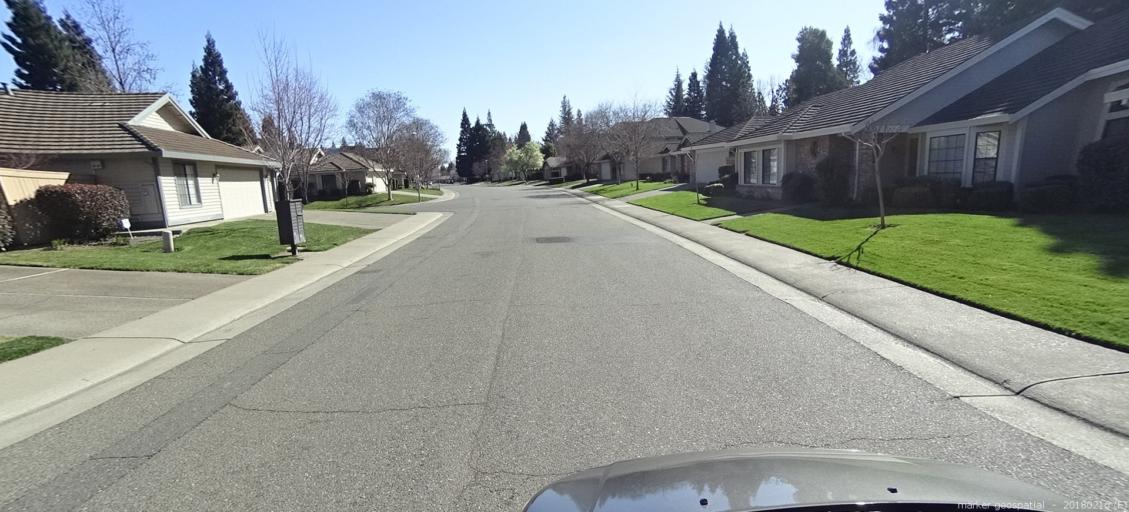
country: US
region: California
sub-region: Sacramento County
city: Gold River
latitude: 38.6234
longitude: -121.2490
